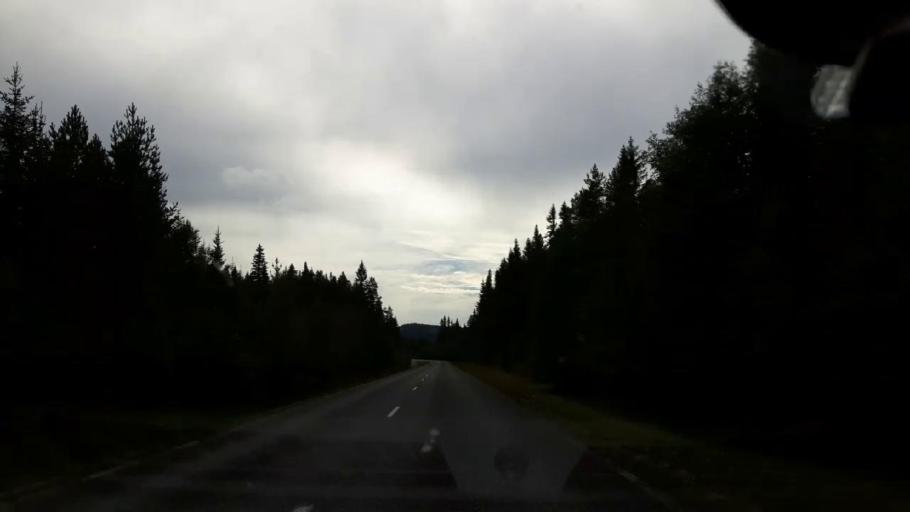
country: SE
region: Jaemtland
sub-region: Ragunda Kommun
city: Hammarstrand
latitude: 63.0782
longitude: 15.9166
